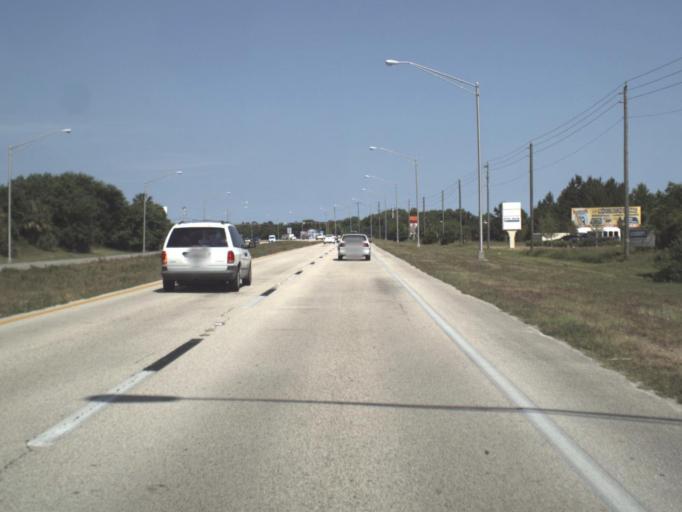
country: US
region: Florida
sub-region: Saint Johns County
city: Saint Augustine South
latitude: 29.8634
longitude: -81.2935
